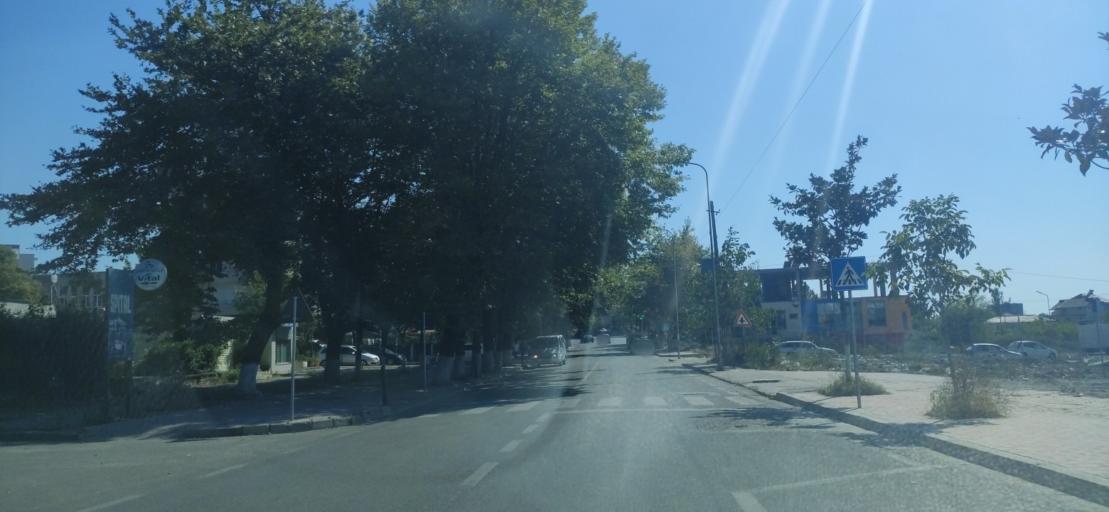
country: AL
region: Lezhe
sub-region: Rrethi i Kurbinit
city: Lac
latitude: 41.6392
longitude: 19.7131
